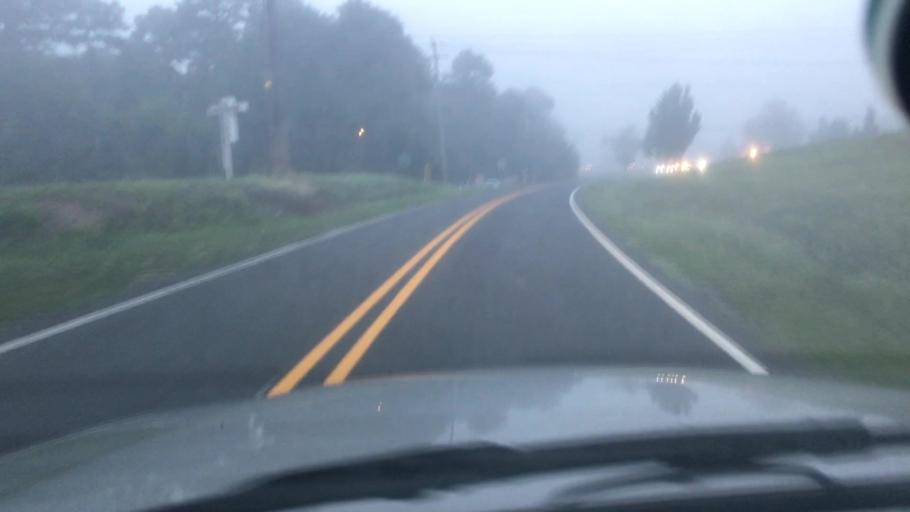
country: US
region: North Carolina
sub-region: Cumberland County
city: Fayetteville
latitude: 35.0092
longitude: -78.8973
